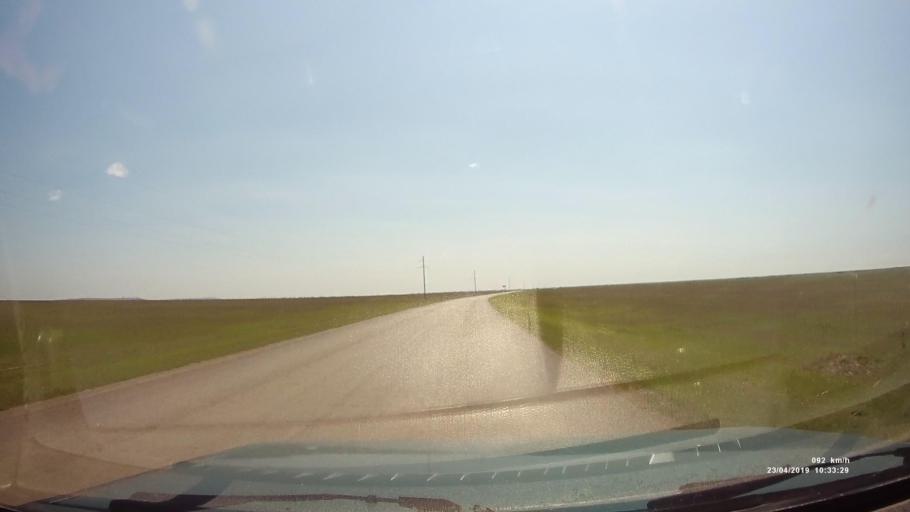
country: RU
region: Kalmykiya
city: Yashalta
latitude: 46.5731
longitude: 42.5972
